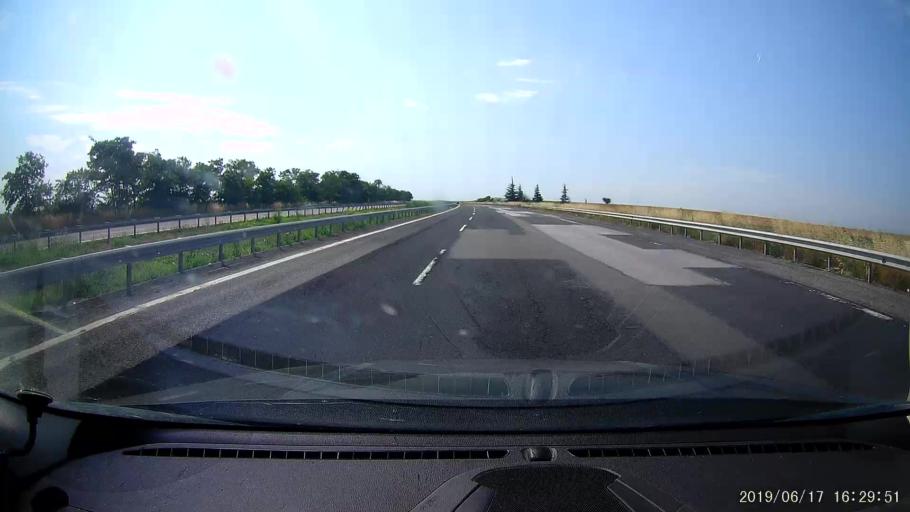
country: TR
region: Tekirdag
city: Beyazkoy
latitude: 41.3393
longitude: 27.6705
